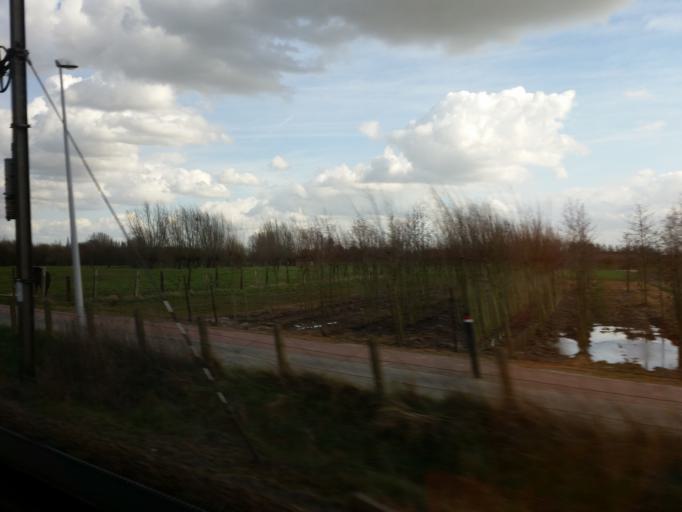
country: BE
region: Flanders
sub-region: Provincie Oost-Vlaanderen
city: Wichelen
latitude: 51.0027
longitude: 3.9381
